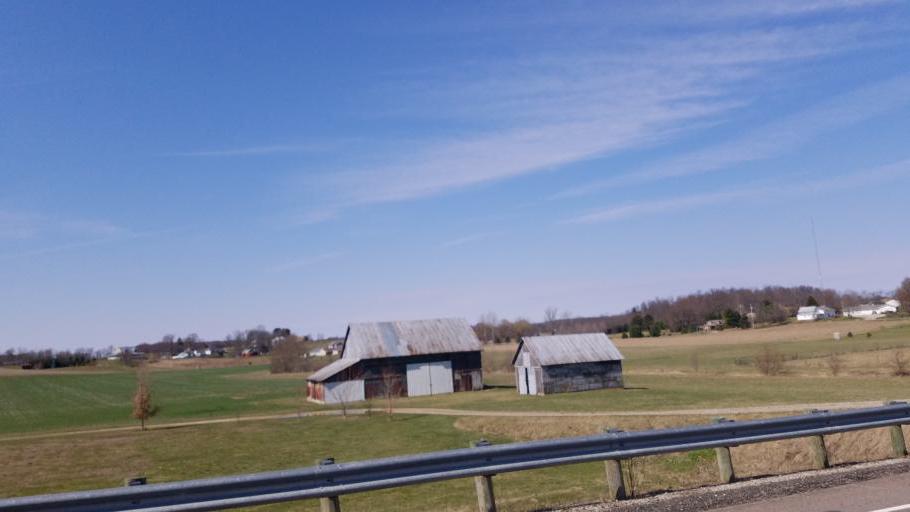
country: US
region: Ohio
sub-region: Knox County
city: Fredericktown
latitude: 40.5290
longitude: -82.5462
